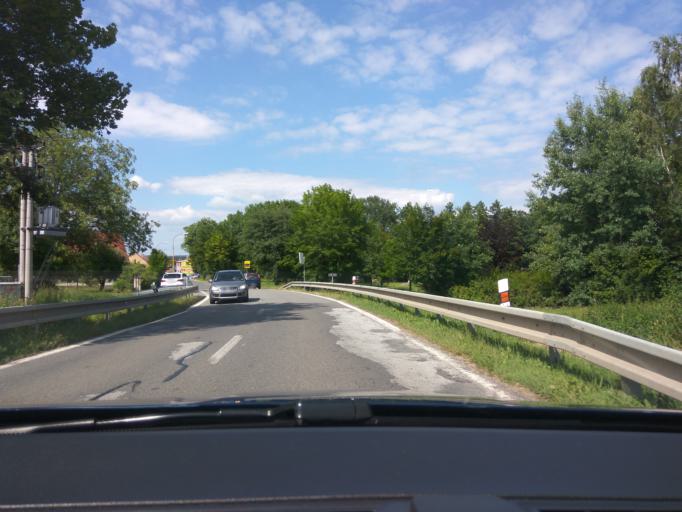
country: CZ
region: Jihocesky
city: Milevsko
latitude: 49.4431
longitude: 14.3598
